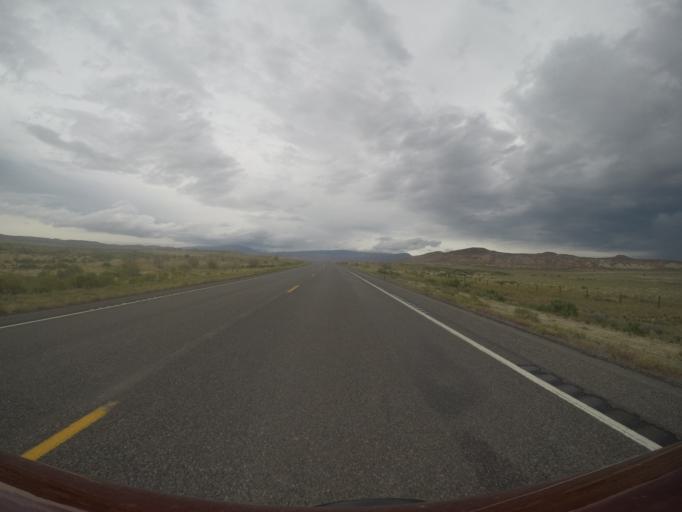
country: US
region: Wyoming
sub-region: Big Horn County
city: Lovell
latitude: 44.9129
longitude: -108.2921
